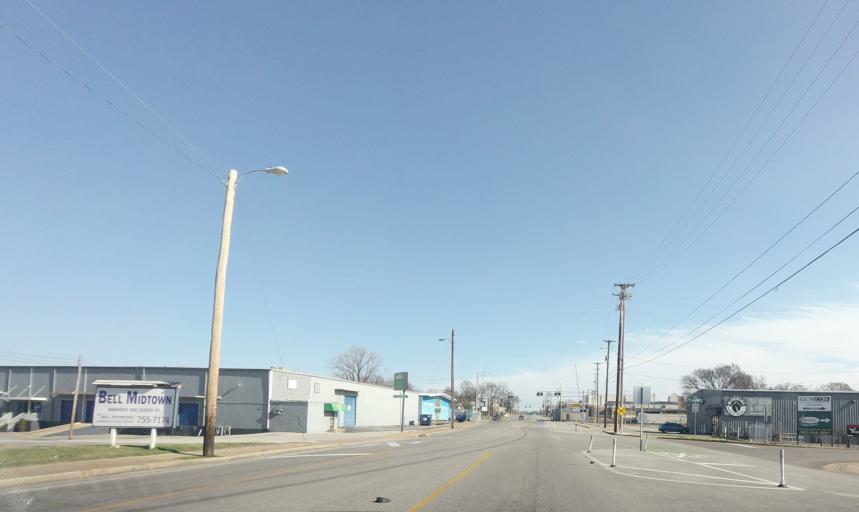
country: US
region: Tennessee
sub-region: Shelby County
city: Memphis
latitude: 35.1475
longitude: -89.9695
